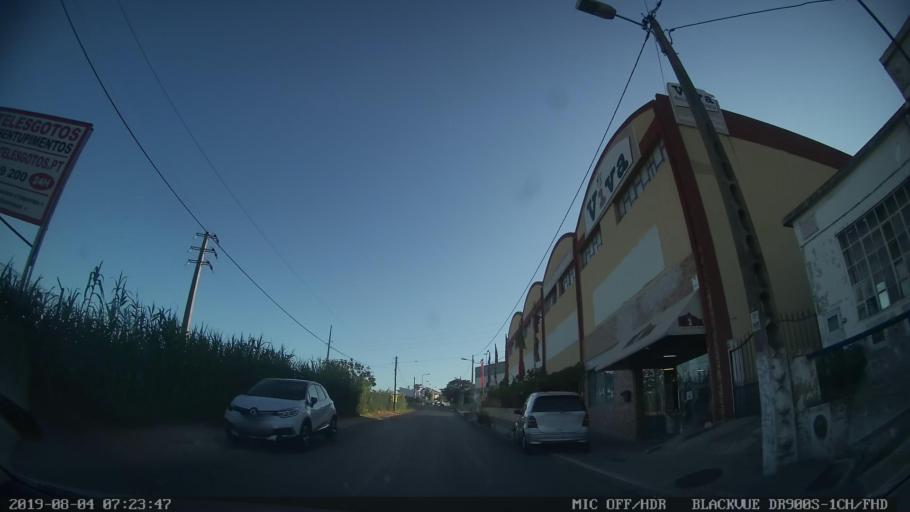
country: PT
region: Lisbon
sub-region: Loures
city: Santa Iria da Azoia
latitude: 38.8509
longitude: -9.0767
